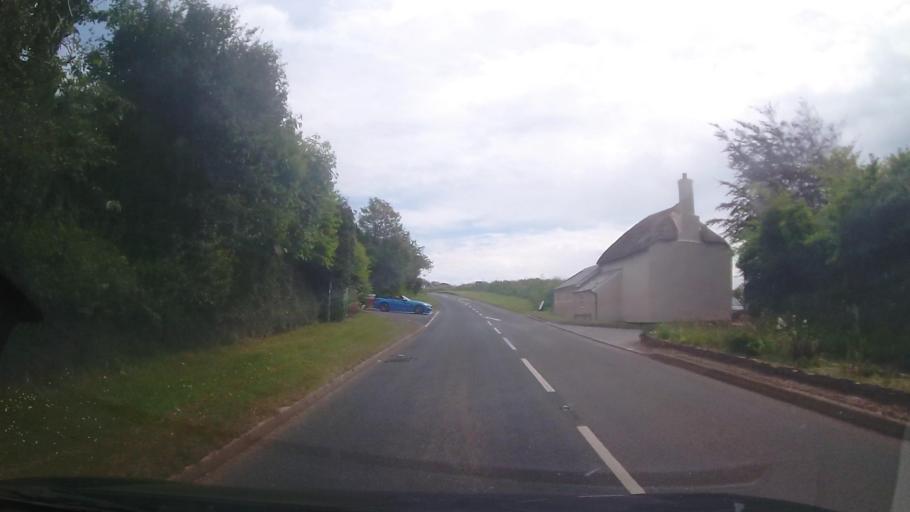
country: GB
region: England
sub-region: Devon
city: Kingsbridge
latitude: 50.2704
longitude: -3.7470
